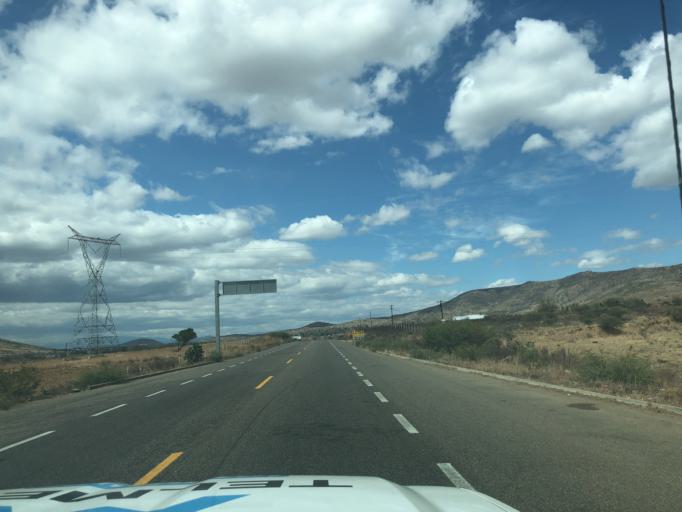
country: MX
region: Oaxaca
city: San Martin de los Canseco
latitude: 16.6345
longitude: -96.7396
